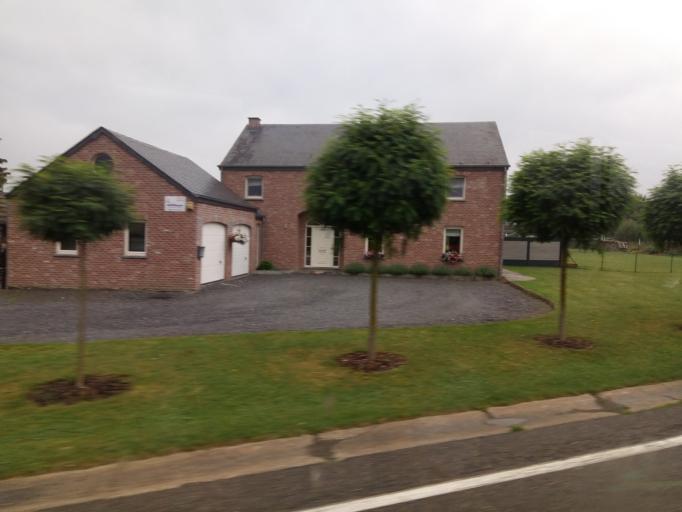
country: BE
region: Wallonia
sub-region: Province du Luxembourg
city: Hotton
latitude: 50.2752
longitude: 5.4390
